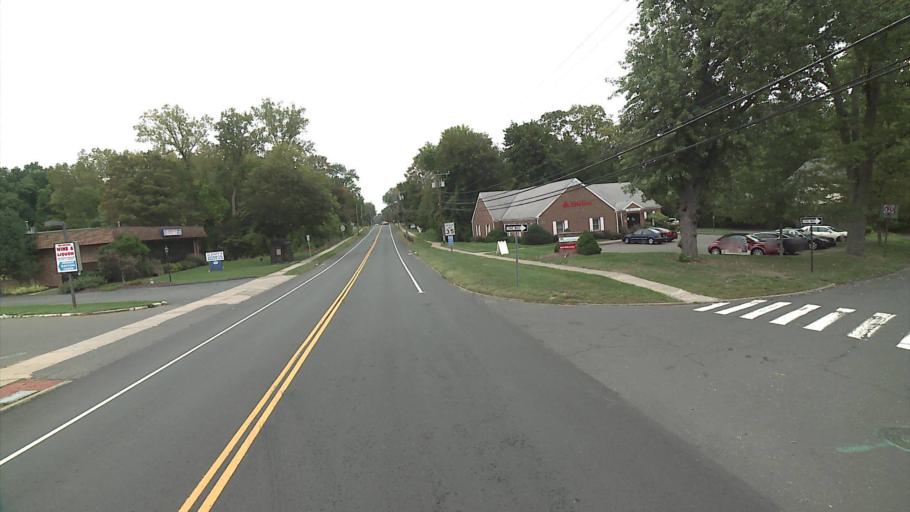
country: US
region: Connecticut
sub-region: Hartford County
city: Windsor
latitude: 41.8562
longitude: -72.6497
